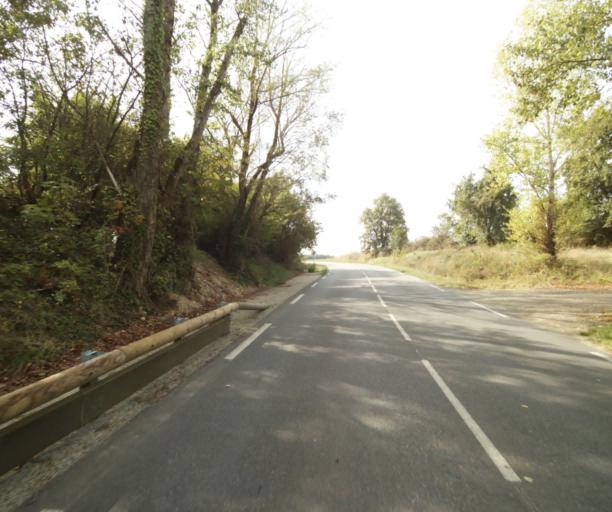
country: FR
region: Midi-Pyrenees
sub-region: Departement du Tarn-et-Garonne
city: Orgueil
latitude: 43.9137
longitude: 1.3957
